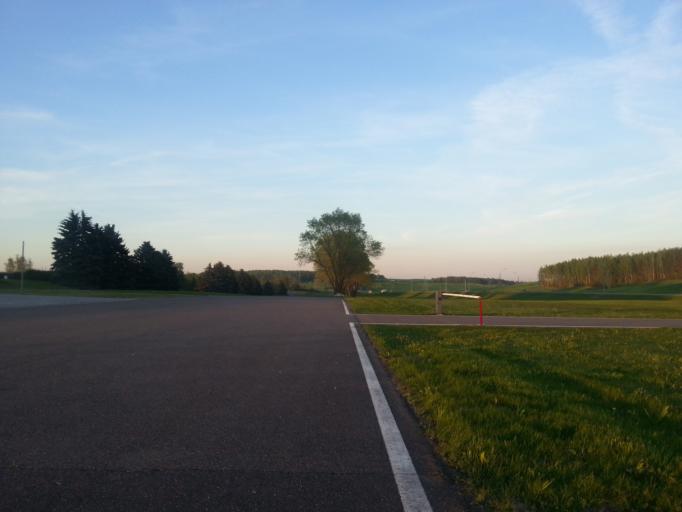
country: BY
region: Minsk
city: Slabada
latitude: 54.0178
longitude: 27.8985
